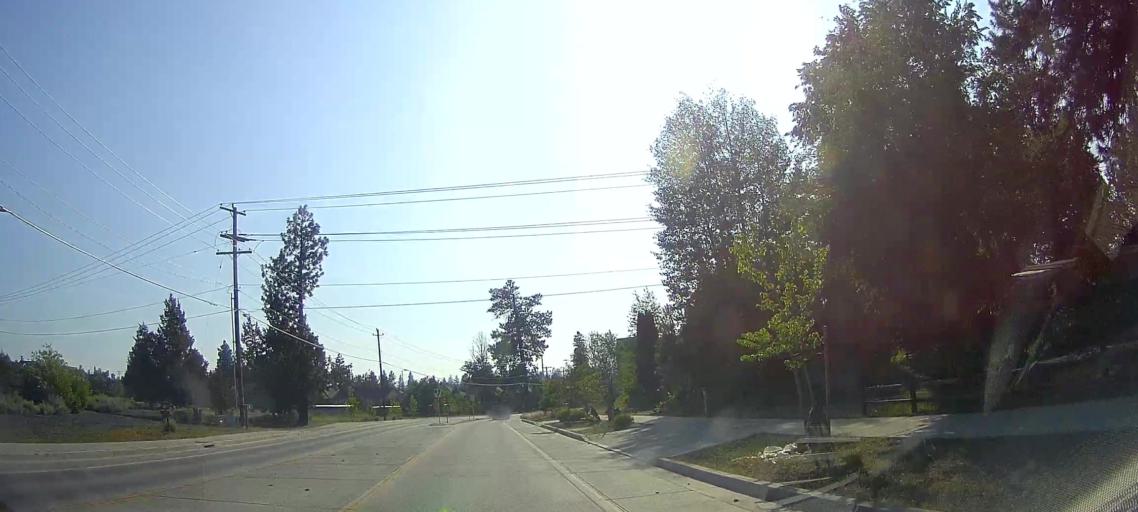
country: US
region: Oregon
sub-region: Deschutes County
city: Bend
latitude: 44.0385
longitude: -121.3000
